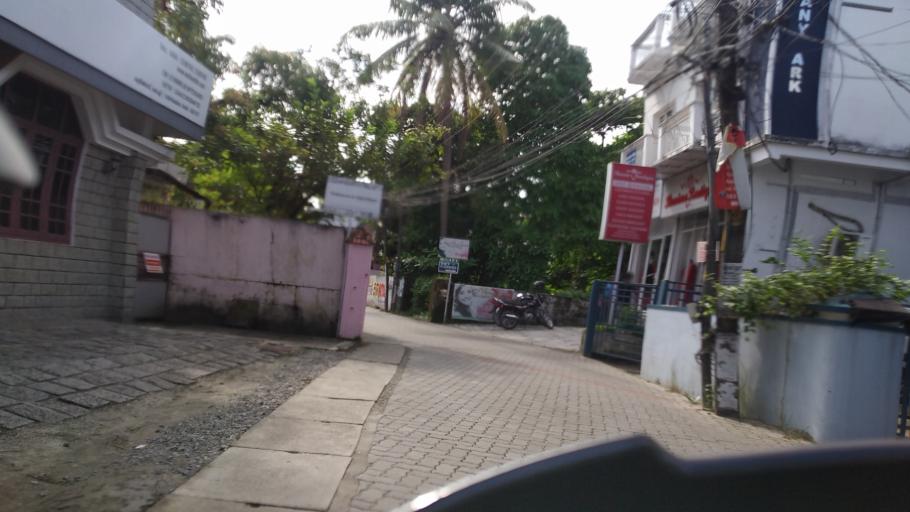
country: IN
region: Kerala
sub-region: Ernakulam
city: Cochin
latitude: 9.9867
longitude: 76.2976
